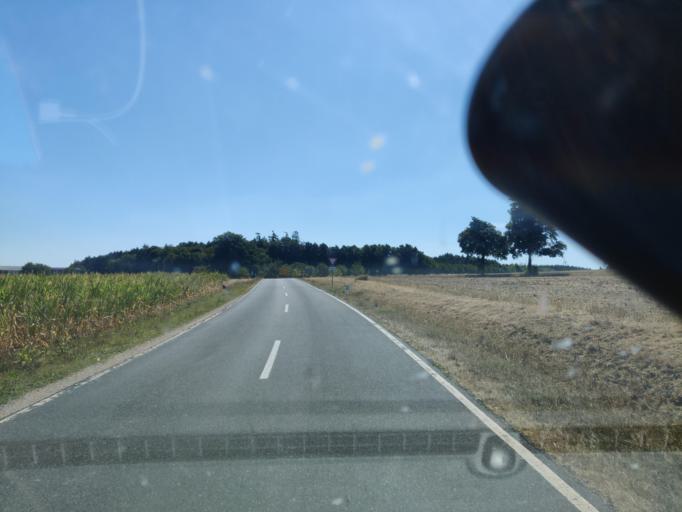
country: DE
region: Bavaria
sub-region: Regierungsbezirk Mittelfranken
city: Thalmassing
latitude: 49.0734
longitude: 11.1982
